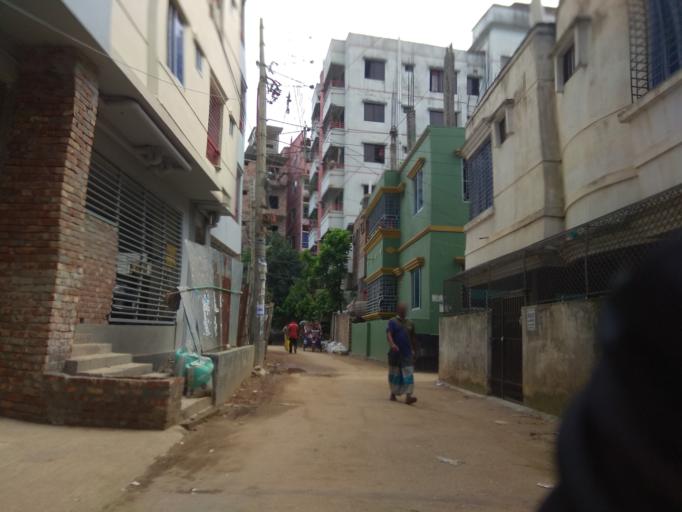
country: BD
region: Dhaka
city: Tungi
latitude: 23.8240
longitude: 90.3880
